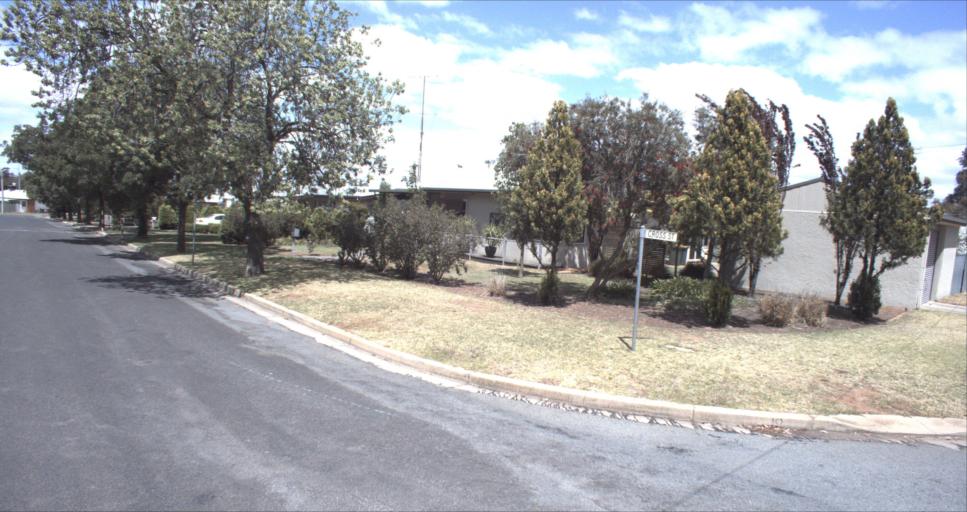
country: AU
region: New South Wales
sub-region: Leeton
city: Leeton
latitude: -34.5623
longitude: 146.3962
